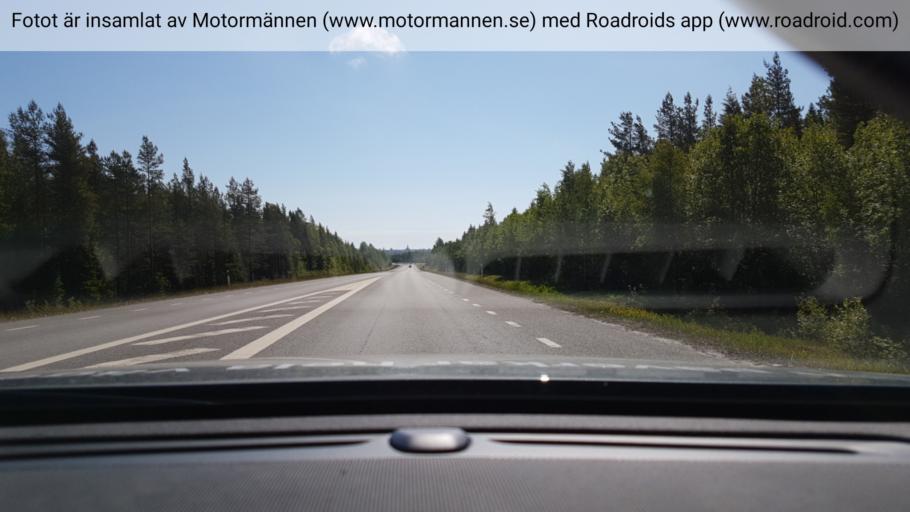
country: SE
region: Vaesterbotten
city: Obbola
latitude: 63.7136
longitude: 20.3115
